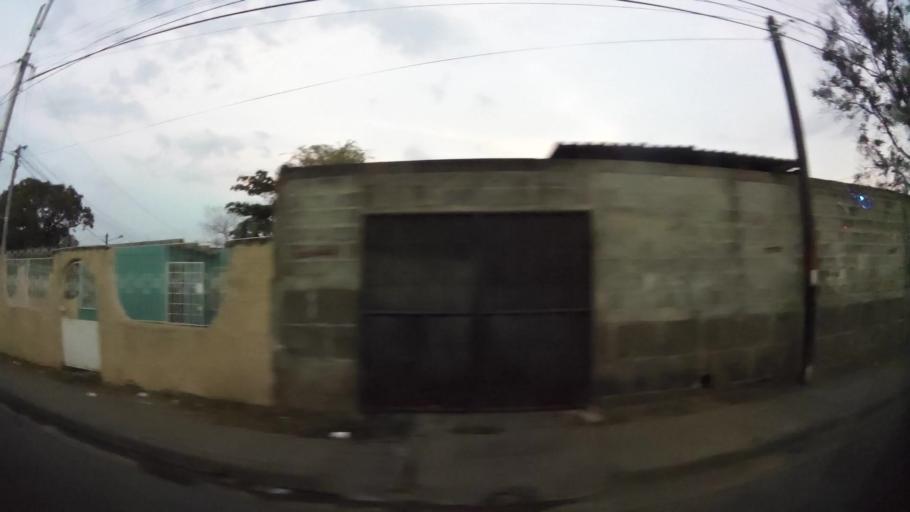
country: NI
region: Managua
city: Managua
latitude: 12.1290
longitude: -86.2399
